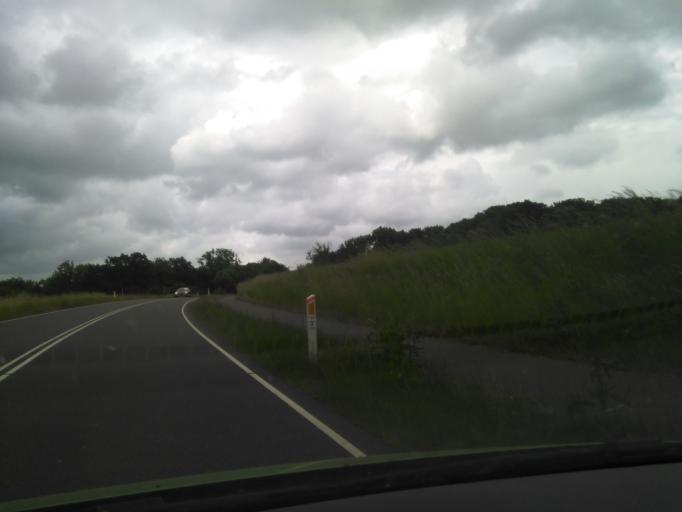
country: DK
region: Capital Region
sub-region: Bornholm Kommune
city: Akirkeby
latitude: 55.2330
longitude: 14.8765
